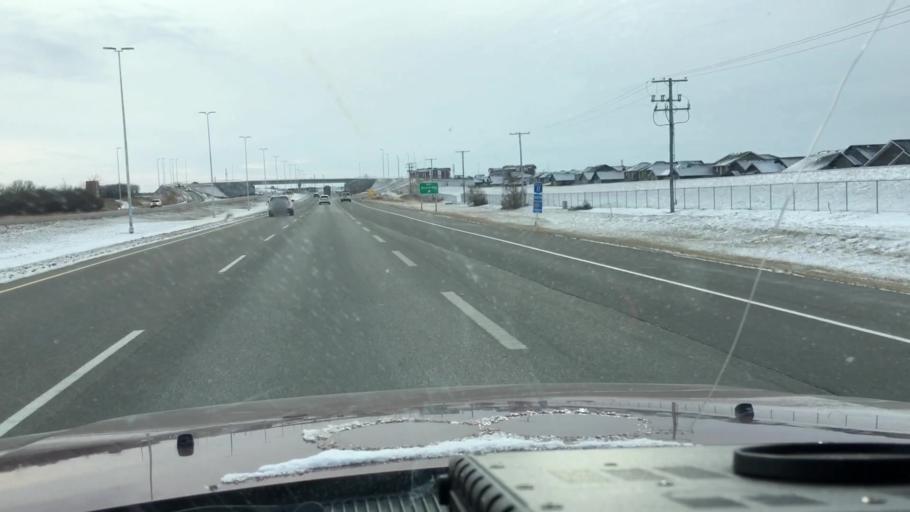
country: CA
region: Saskatchewan
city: Saskatoon
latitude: 52.0830
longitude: -106.6049
